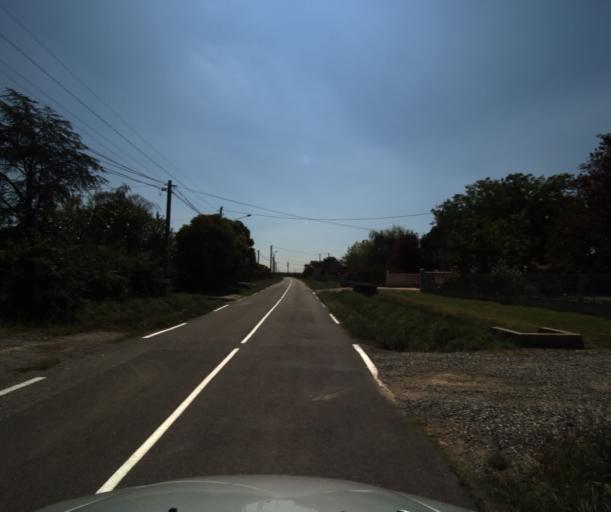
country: FR
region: Midi-Pyrenees
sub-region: Departement de la Haute-Garonne
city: Labastidette
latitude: 43.4393
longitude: 1.2571
